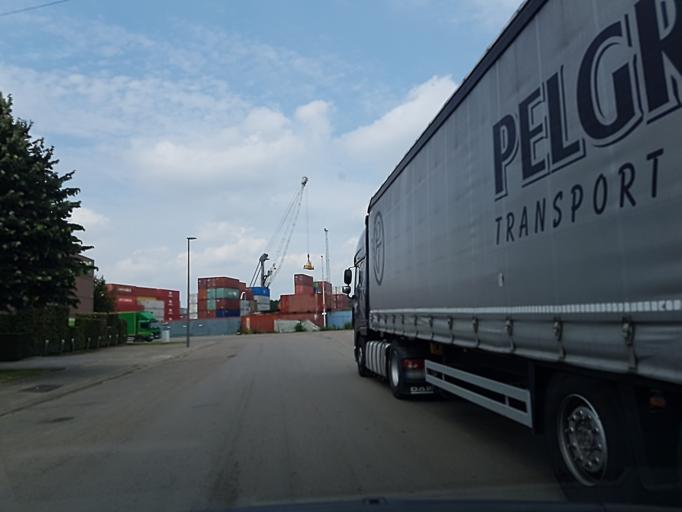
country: BE
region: Flanders
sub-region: Provincie Antwerpen
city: Schoten
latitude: 51.2373
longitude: 4.4690
